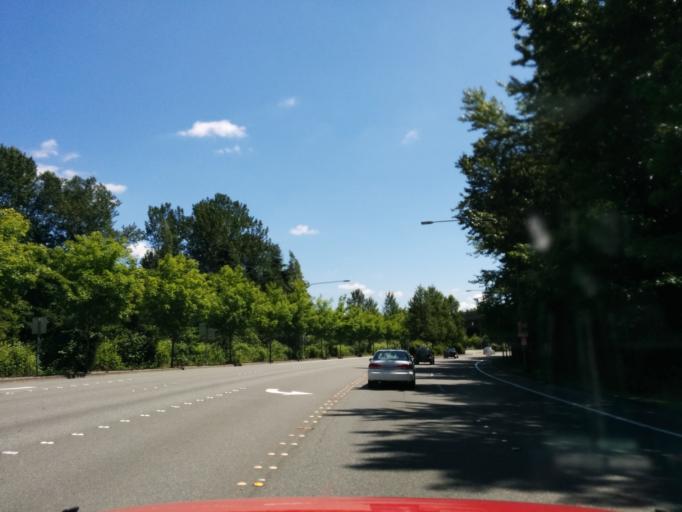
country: US
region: Washington
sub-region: King County
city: Redmond
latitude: 47.6688
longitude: -122.1285
